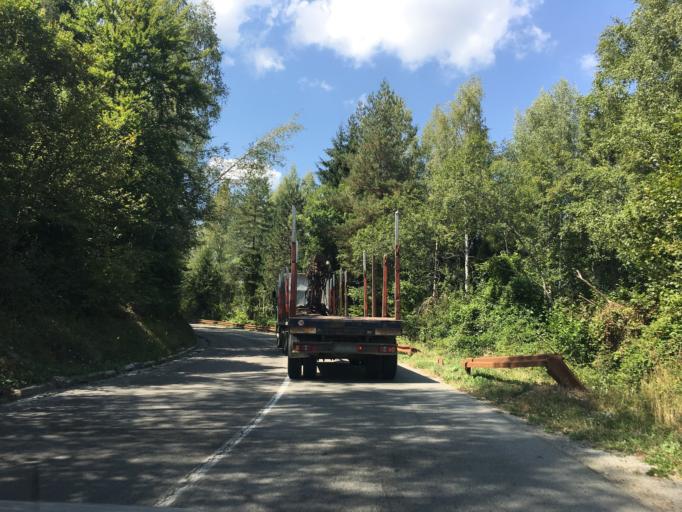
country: RS
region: Central Serbia
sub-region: Zlatiborski Okrug
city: Prijepolje
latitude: 43.3294
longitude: 19.5405
